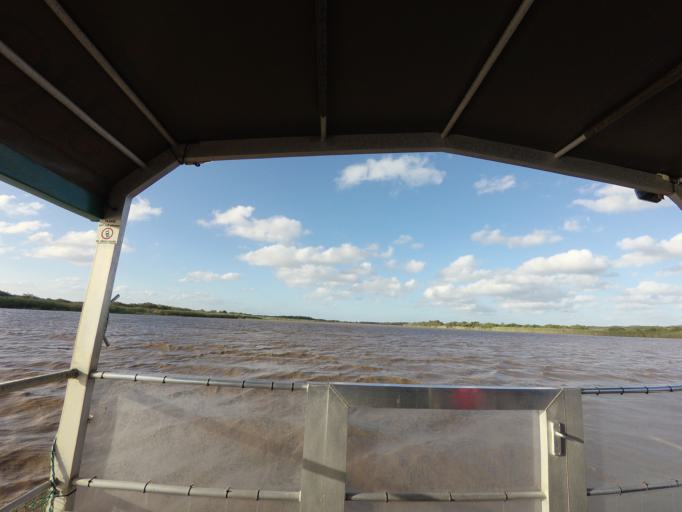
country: ZA
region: KwaZulu-Natal
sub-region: uMkhanyakude District Municipality
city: Mtubatuba
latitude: -28.3551
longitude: 32.4082
